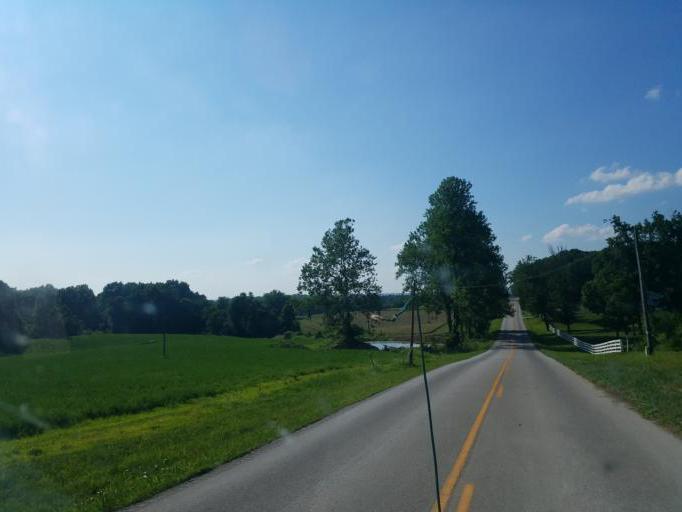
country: US
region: Kentucky
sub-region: Hart County
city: Munfordville
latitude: 37.3158
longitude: -86.0595
